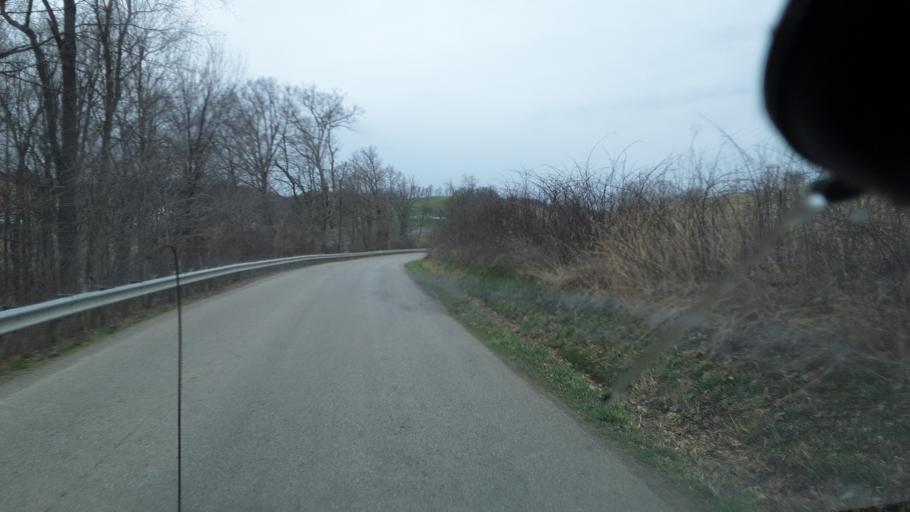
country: US
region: Ohio
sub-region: Coshocton County
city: West Lafayette
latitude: 40.3302
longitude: -81.6901
